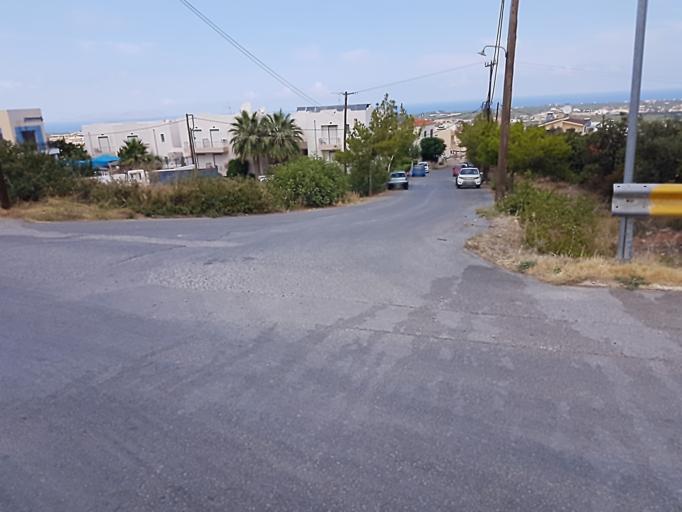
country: GR
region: Crete
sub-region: Nomos Irakleiou
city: Limin Khersonisou
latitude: 35.3055
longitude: 25.3720
